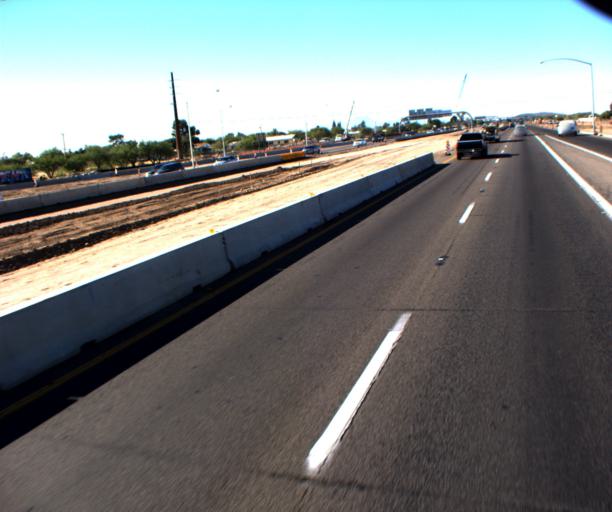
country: US
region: Arizona
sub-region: Pima County
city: South Tucson
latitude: 32.1760
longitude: -110.9858
